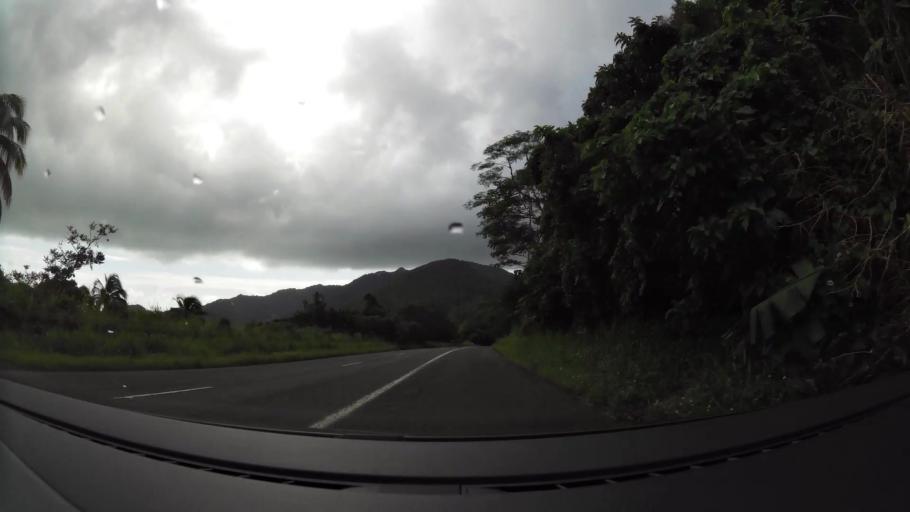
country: GP
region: Guadeloupe
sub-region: Guadeloupe
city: Gourbeyre
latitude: 15.9969
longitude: -61.6780
